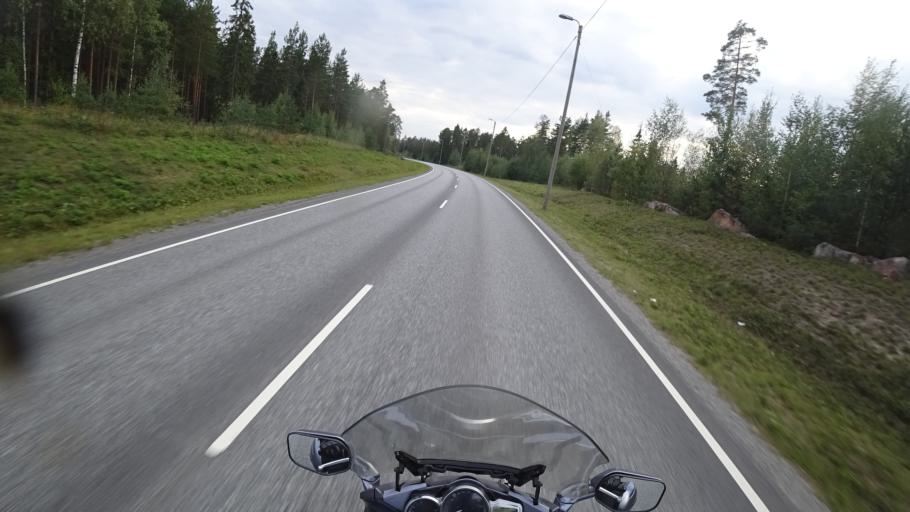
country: FI
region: Uusimaa
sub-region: Raaseporin
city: Karis
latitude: 60.0684
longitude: 23.6320
